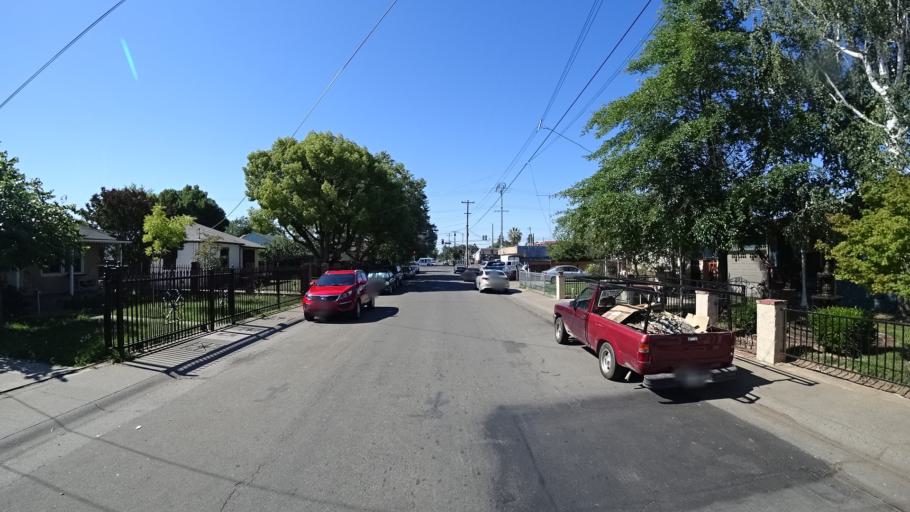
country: US
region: California
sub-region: Sacramento County
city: Parkway
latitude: 38.5256
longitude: -121.4773
